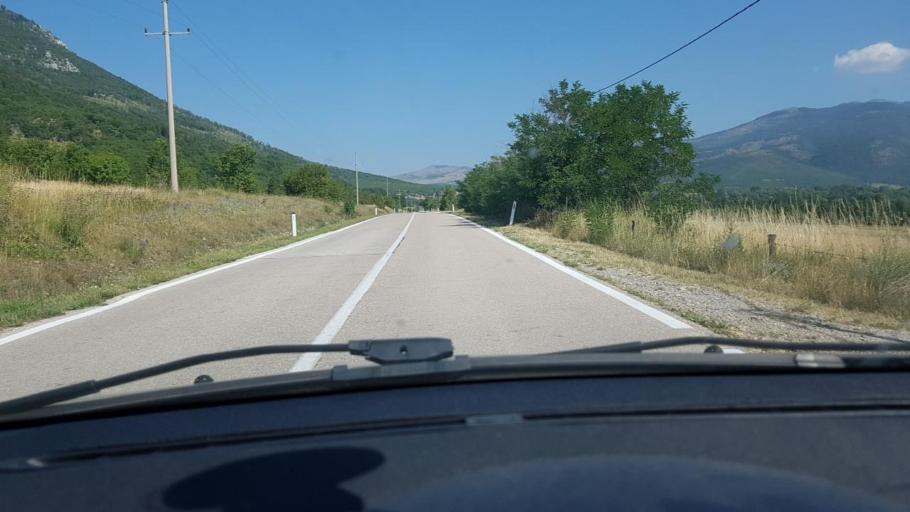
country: BA
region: Federation of Bosnia and Herzegovina
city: Bosansko Grahovo
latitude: 44.0613
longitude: 16.5831
